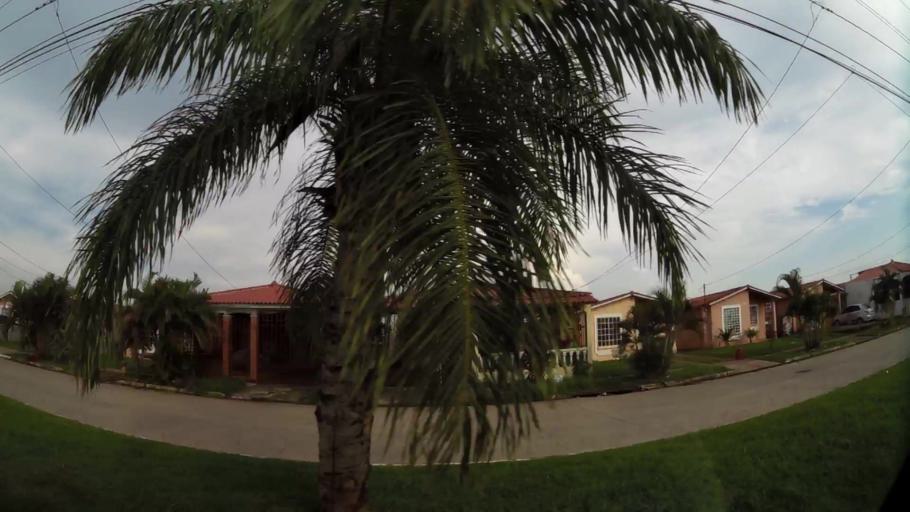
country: PA
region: Panama
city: Tocumen
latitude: 9.0728
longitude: -79.3648
